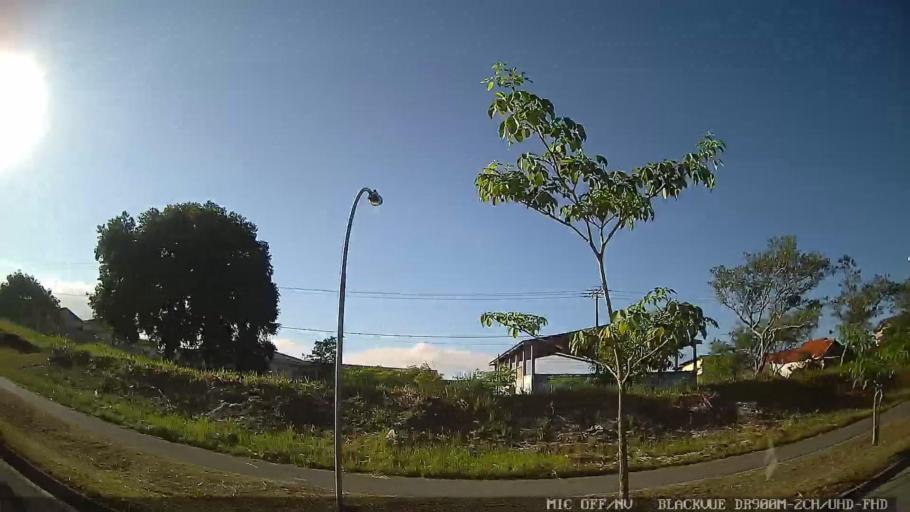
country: BR
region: Sao Paulo
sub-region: Peruibe
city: Peruibe
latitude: -24.3035
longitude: -46.9904
